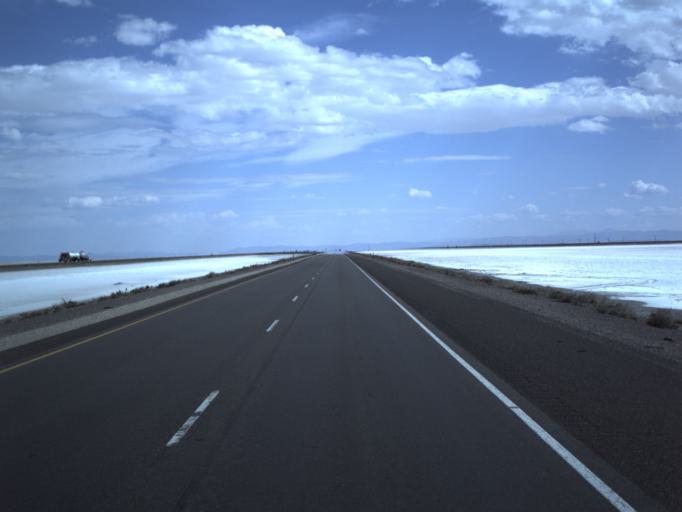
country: US
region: Utah
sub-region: Tooele County
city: Wendover
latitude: 40.7354
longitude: -113.7009
